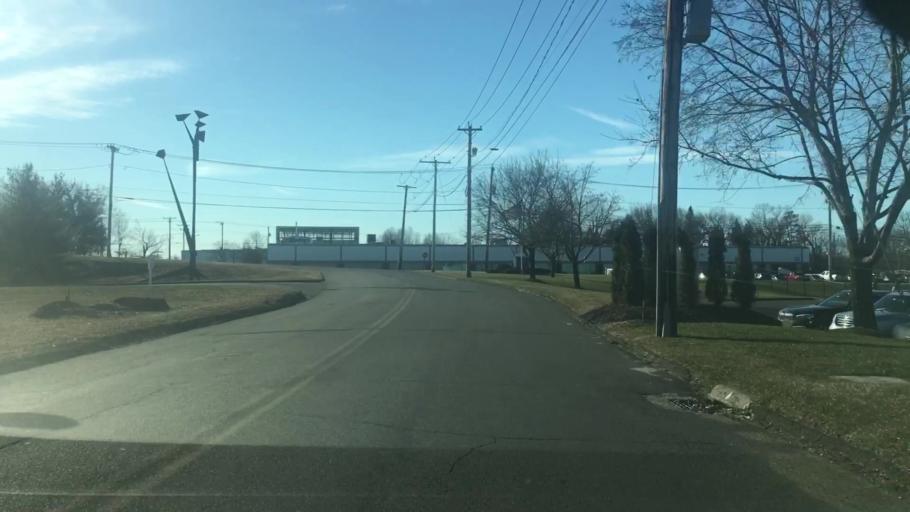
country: US
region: Connecticut
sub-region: New Haven County
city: North Haven
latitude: 41.4194
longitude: -72.8445
